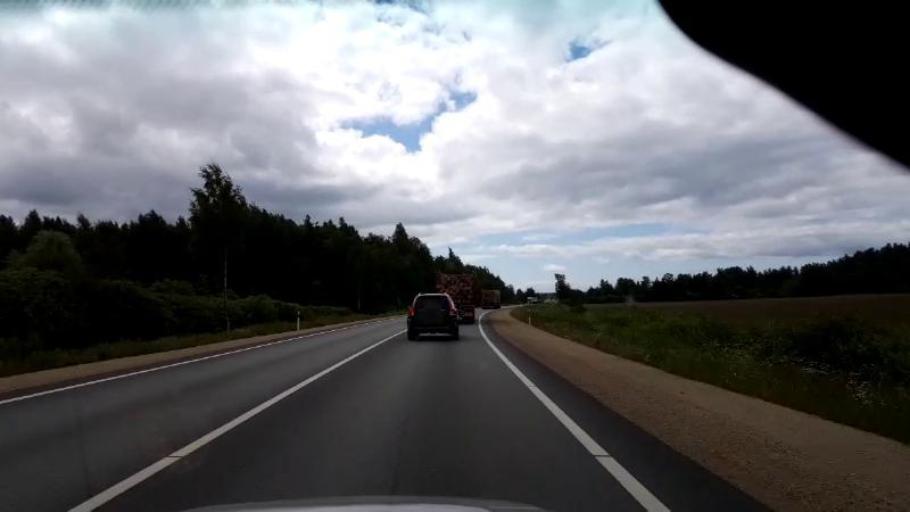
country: LV
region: Salacgrivas
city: Salacgriva
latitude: 57.7269
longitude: 24.3659
